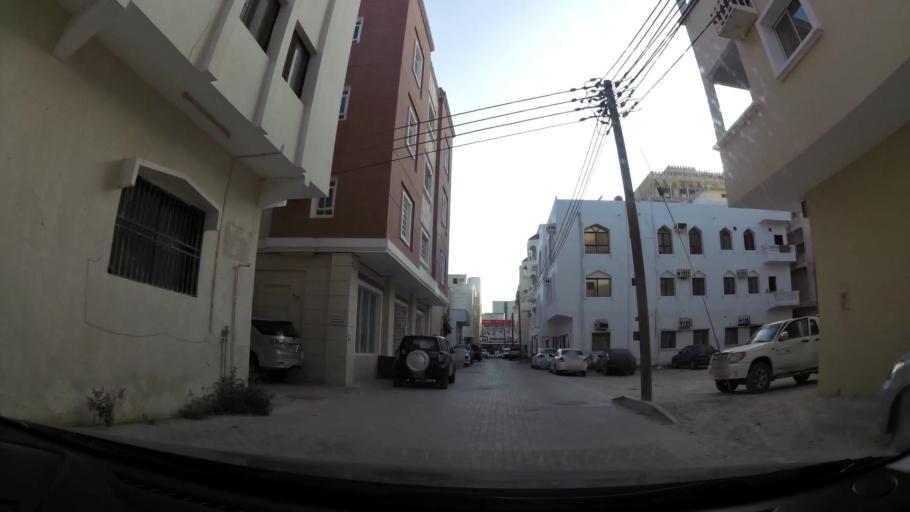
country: OM
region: Zufar
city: Salalah
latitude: 17.0152
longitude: 54.0942
